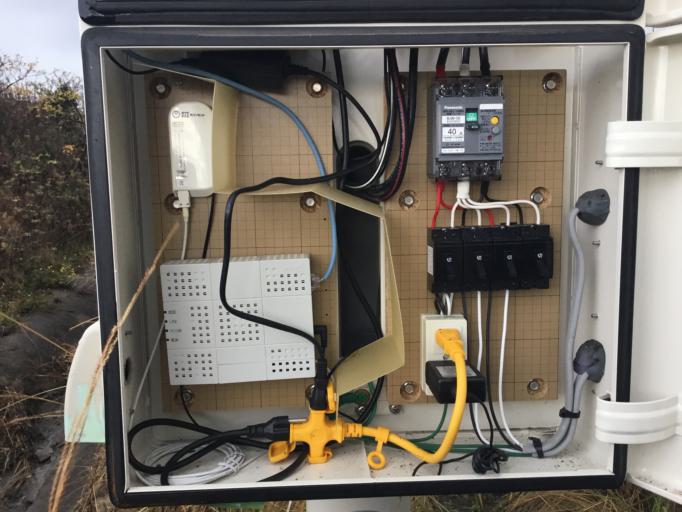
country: JP
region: Wakayama
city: Minato
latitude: 34.2774
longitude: 135.0915
